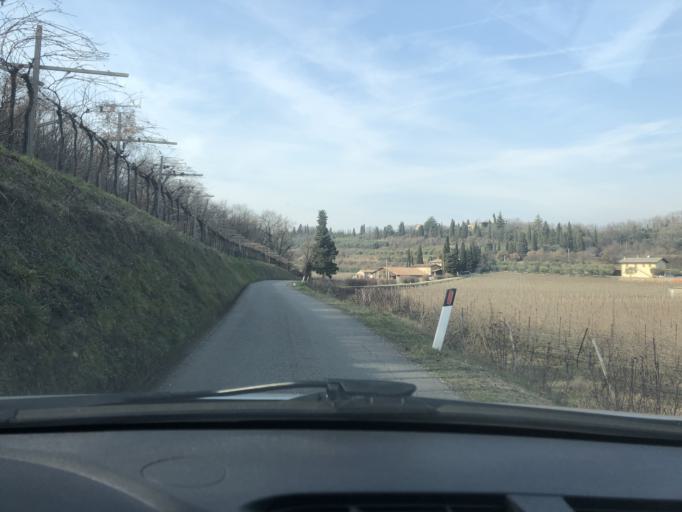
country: IT
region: Veneto
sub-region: Provincia di Verona
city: Costermano
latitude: 45.5678
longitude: 10.7352
